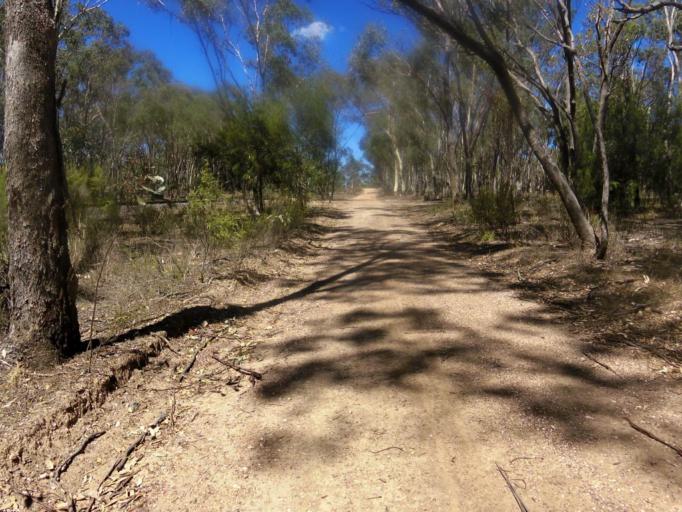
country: AU
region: Victoria
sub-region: Mount Alexander
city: Castlemaine
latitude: -37.0539
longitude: 144.1876
